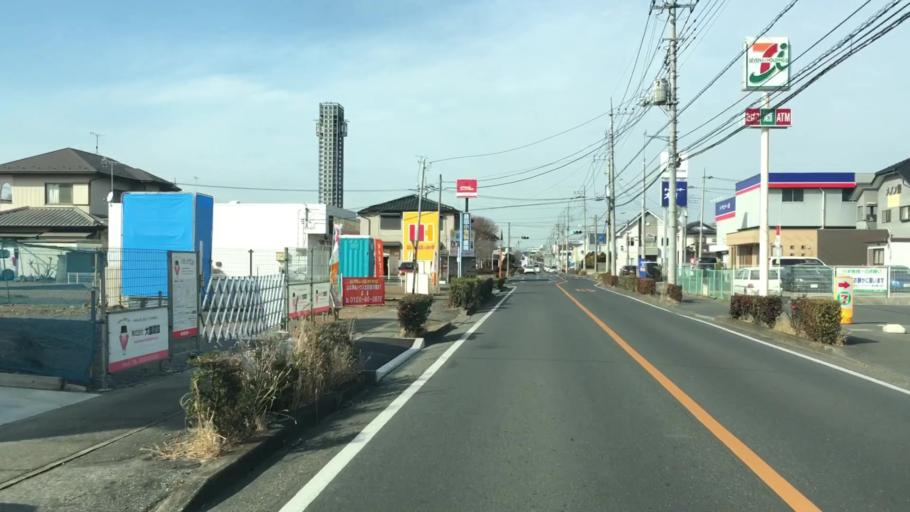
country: JP
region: Saitama
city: Menuma
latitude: 36.2521
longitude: 139.4258
